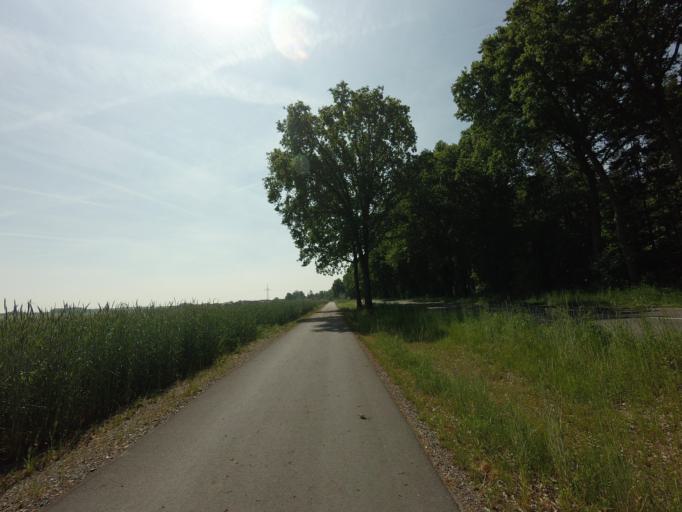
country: DE
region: Lower Saxony
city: Klein Schwulper
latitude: 52.3639
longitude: 10.4279
